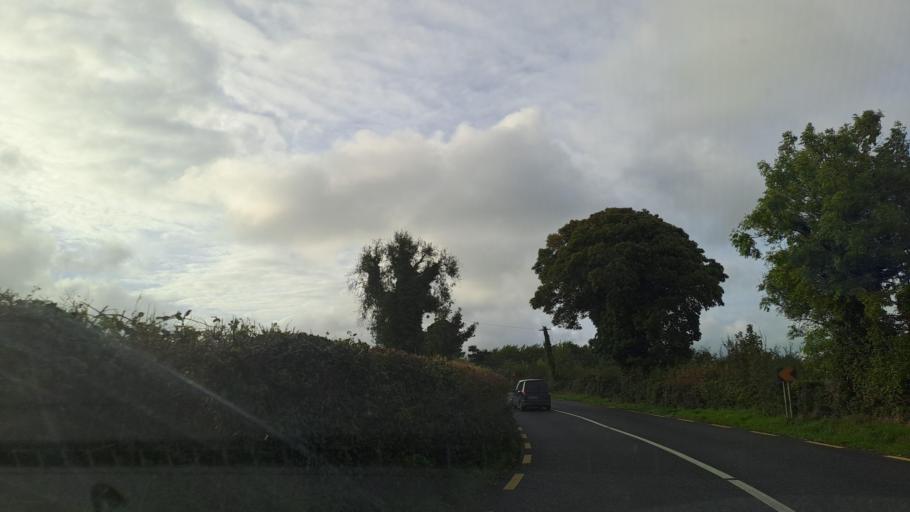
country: IE
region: Ulster
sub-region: An Cabhan
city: Kingscourt
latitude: 53.8305
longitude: -6.7588
